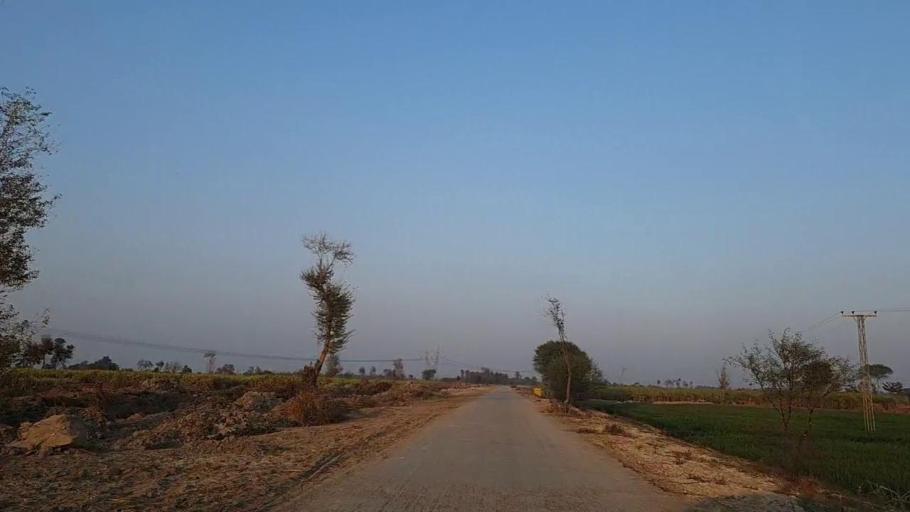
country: PK
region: Sindh
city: Moro
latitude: 26.7633
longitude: 68.0426
